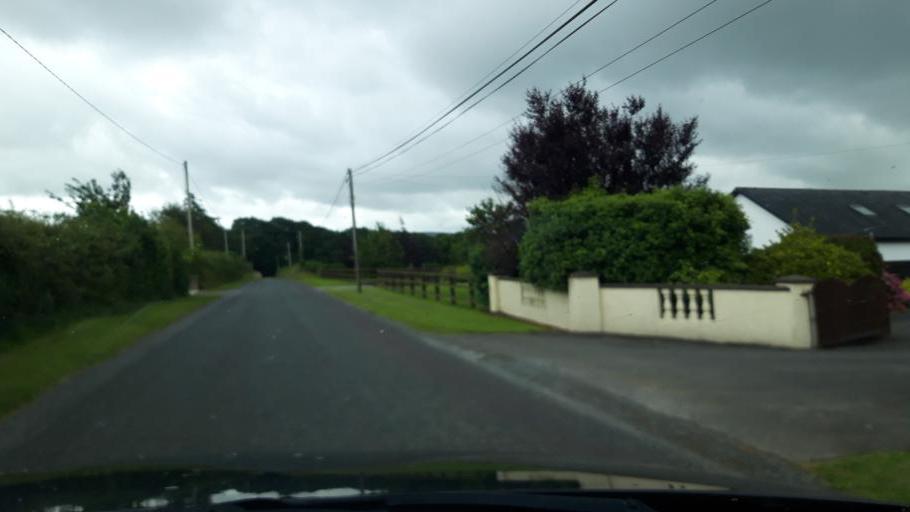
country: IE
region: Munster
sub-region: County Cork
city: Youghal
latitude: 52.1277
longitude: -7.9755
